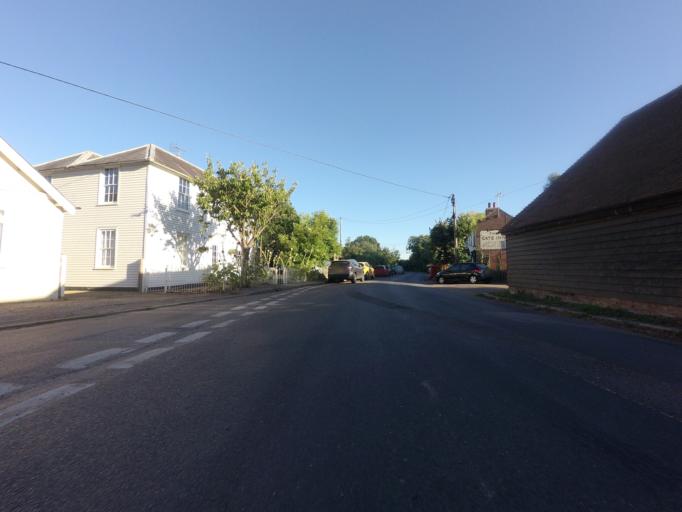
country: GB
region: England
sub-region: Kent
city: Herne Bay
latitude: 51.3461
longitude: 1.1871
